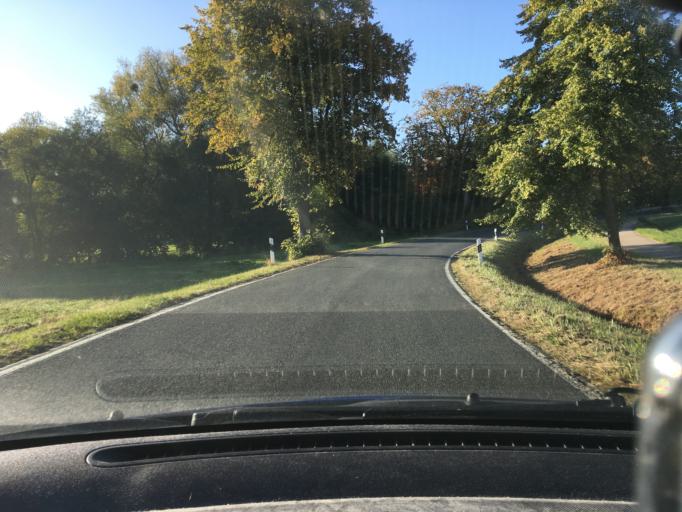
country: DE
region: Lower Saxony
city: Messenkamp
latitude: 52.2135
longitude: 9.3975
